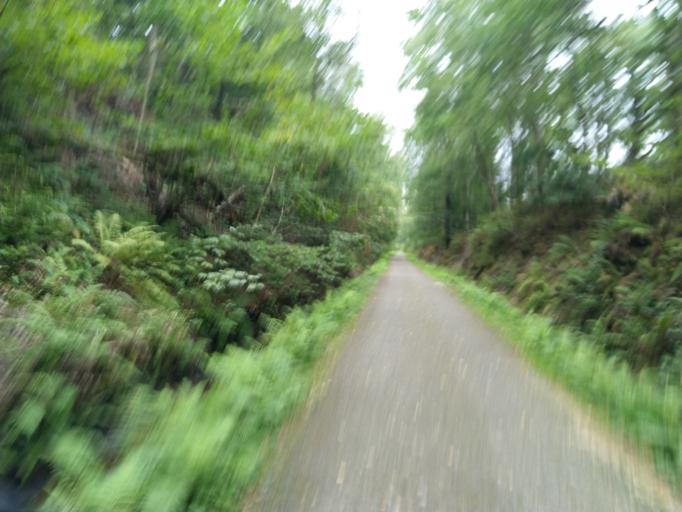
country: BE
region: Wallonia
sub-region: Province de Liege
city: Stavelot
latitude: 50.4179
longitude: 5.9461
